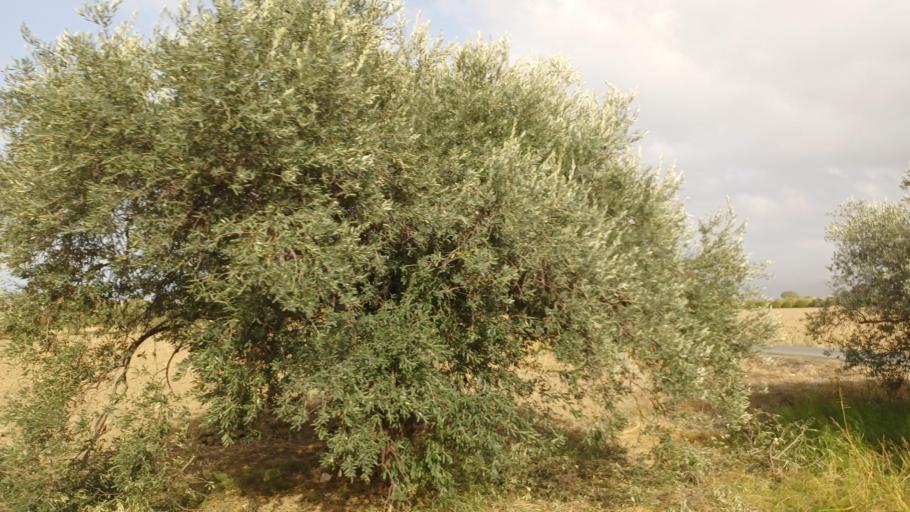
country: CY
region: Pafos
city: Polis
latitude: 35.0383
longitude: 32.4158
